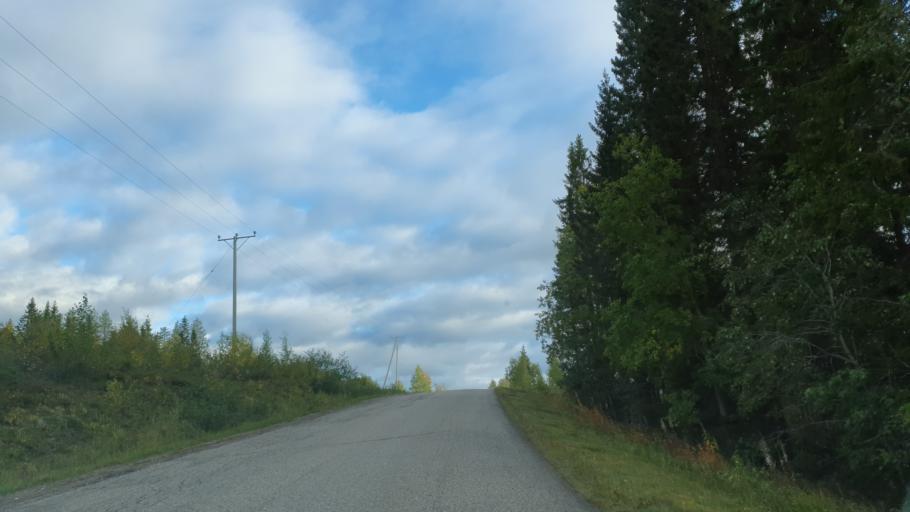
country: FI
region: Kainuu
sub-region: Kehys-Kainuu
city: Kuhmo
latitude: 63.9170
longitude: 30.0704
